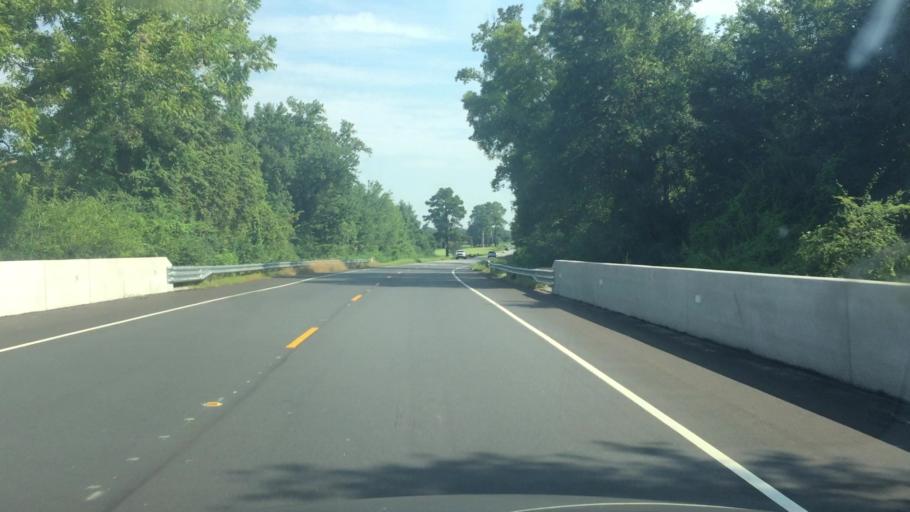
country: US
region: North Carolina
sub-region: Columbus County
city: Chadbourn
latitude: 34.2550
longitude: -78.8182
